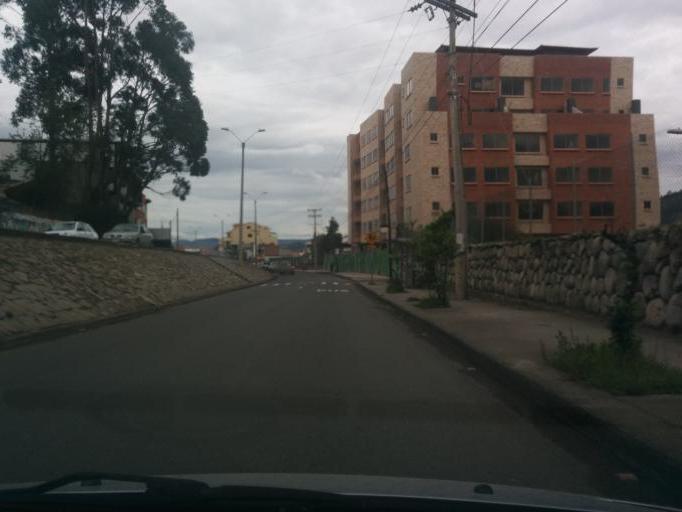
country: EC
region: Azuay
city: Cuenca
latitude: -2.8945
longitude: -78.9713
